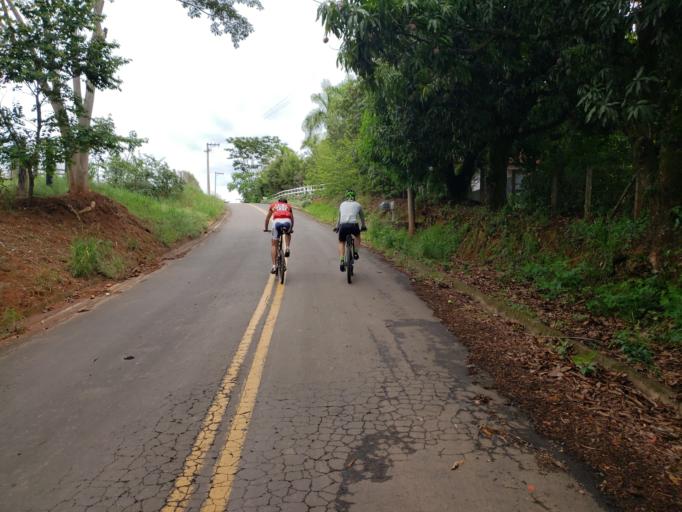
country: BR
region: Sao Paulo
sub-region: Itapira
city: Itapira
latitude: -22.3300
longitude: -46.8201
